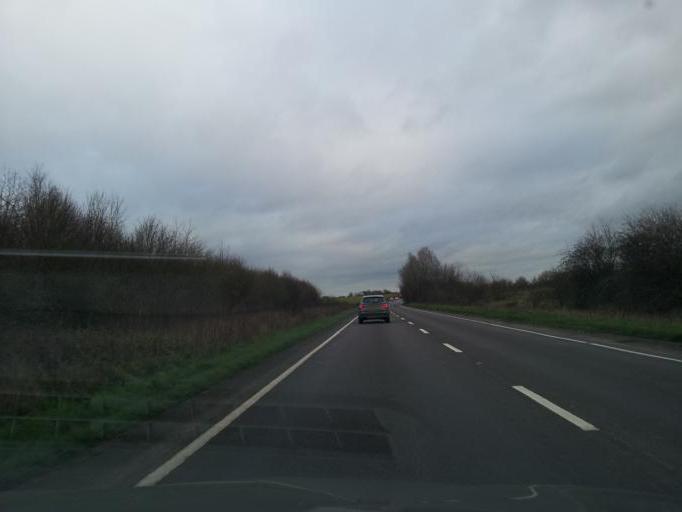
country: GB
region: England
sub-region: Norfolk
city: Diss
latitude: 52.4054
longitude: 1.1868
